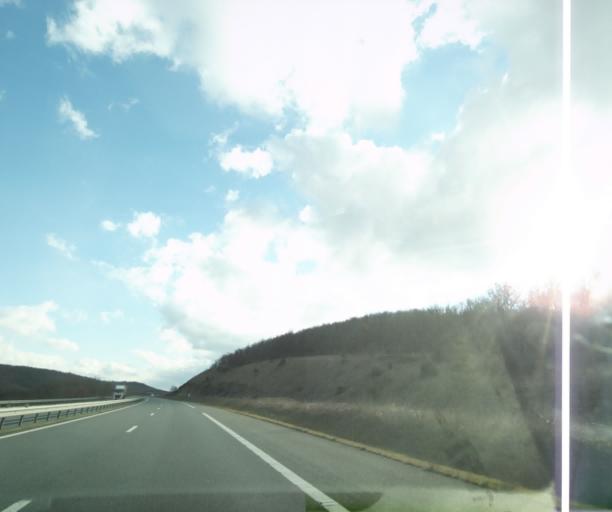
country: FR
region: Midi-Pyrenees
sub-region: Departement du Lot
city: Le Vigan
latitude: 44.7797
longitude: 1.5322
